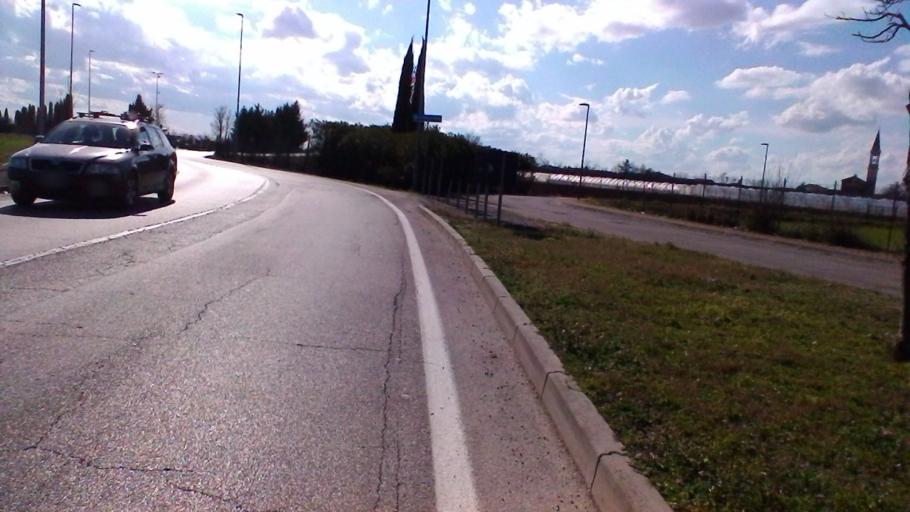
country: IT
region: Veneto
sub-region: Provincia di Verona
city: Alpo
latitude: 45.3733
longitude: 10.9201
